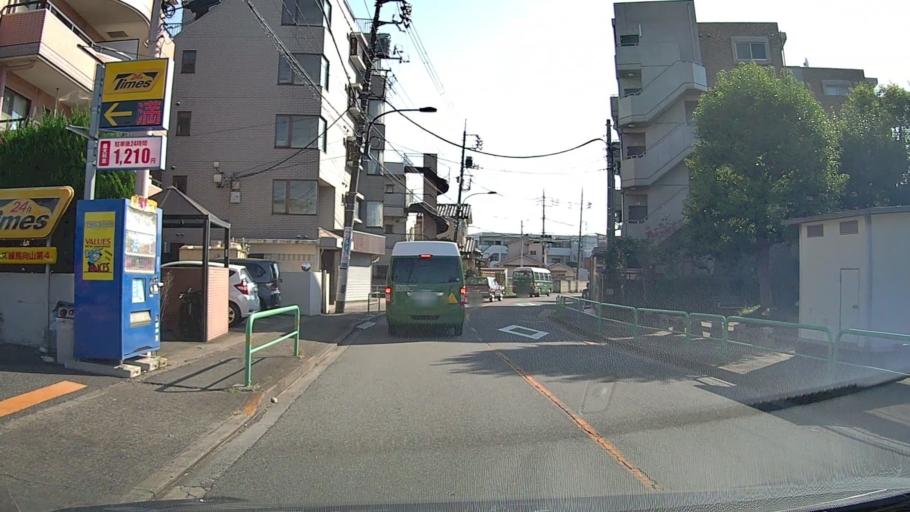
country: JP
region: Saitama
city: Wako
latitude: 35.7450
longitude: 139.6339
